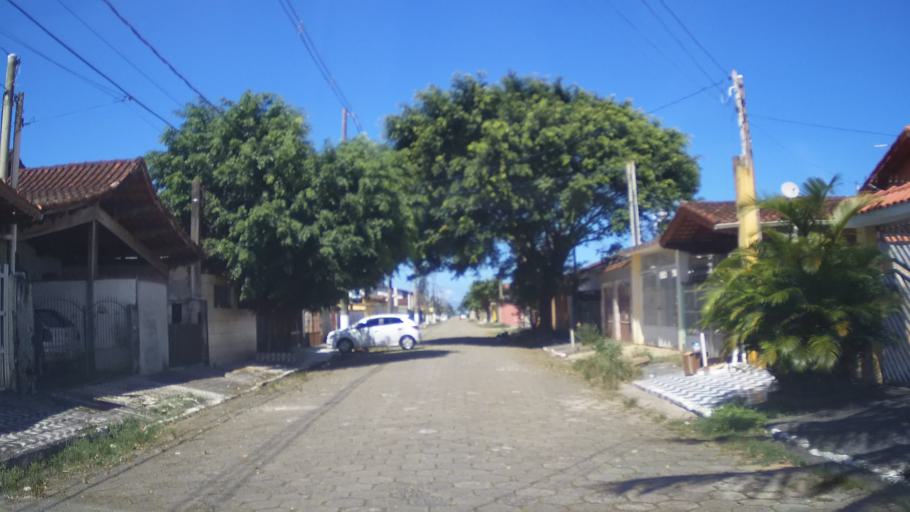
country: BR
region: Sao Paulo
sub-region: Praia Grande
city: Praia Grande
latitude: -24.0400
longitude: -46.5092
